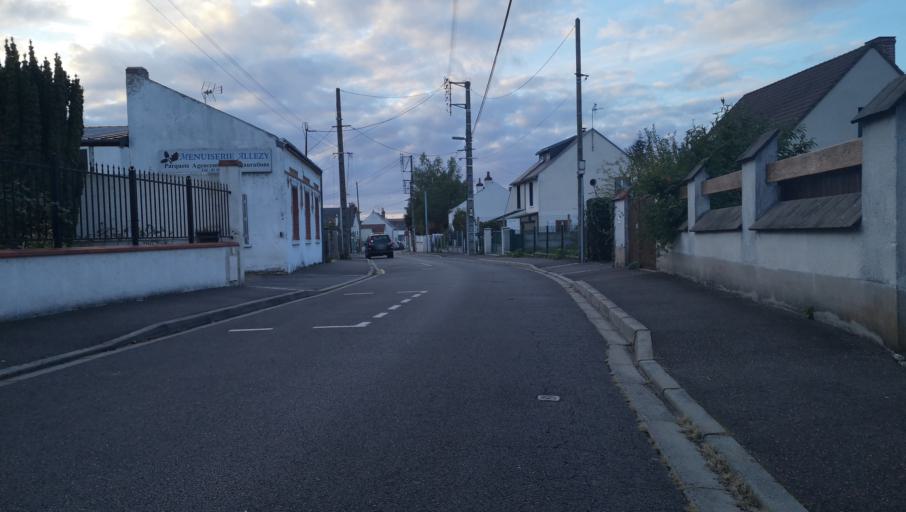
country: FR
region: Centre
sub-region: Departement du Loiret
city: Saint-Jean-de-la-Ruelle
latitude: 47.9047
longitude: 1.8837
